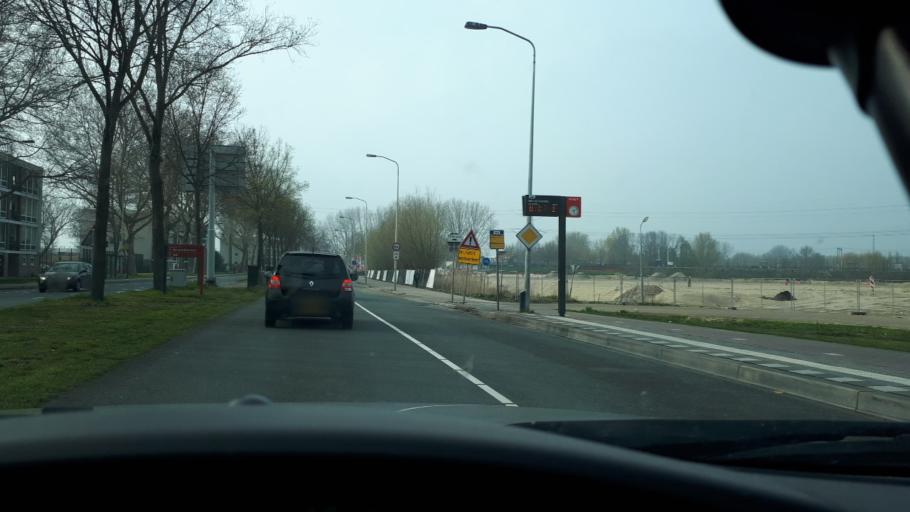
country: NL
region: North Holland
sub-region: Gemeente Zaanstad
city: Zaanstad
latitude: 52.4542
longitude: 4.8216
